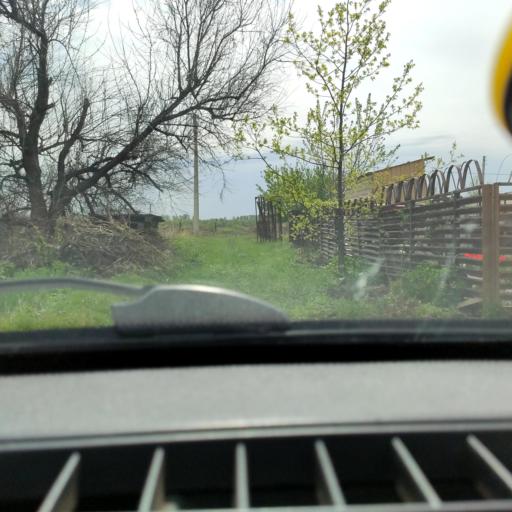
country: RU
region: Samara
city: Tol'yatti
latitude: 53.6968
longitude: 49.4545
